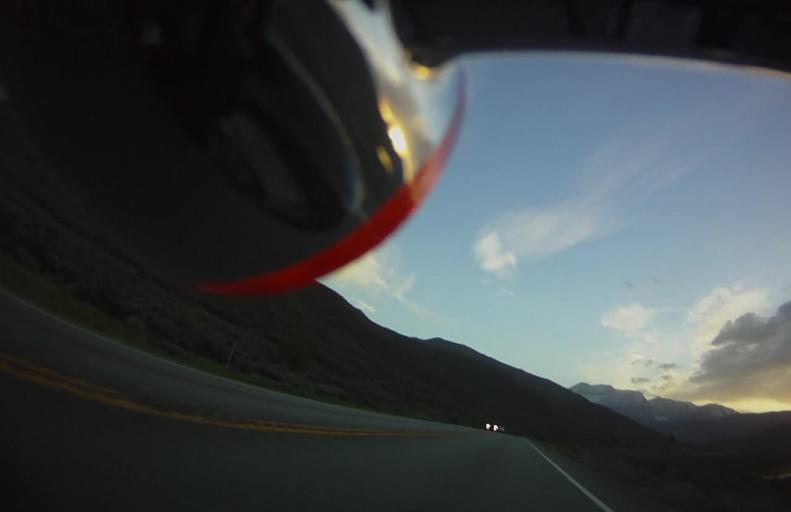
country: US
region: Utah
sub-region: Wasatch County
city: Midway
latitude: 40.4079
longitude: -111.4838
